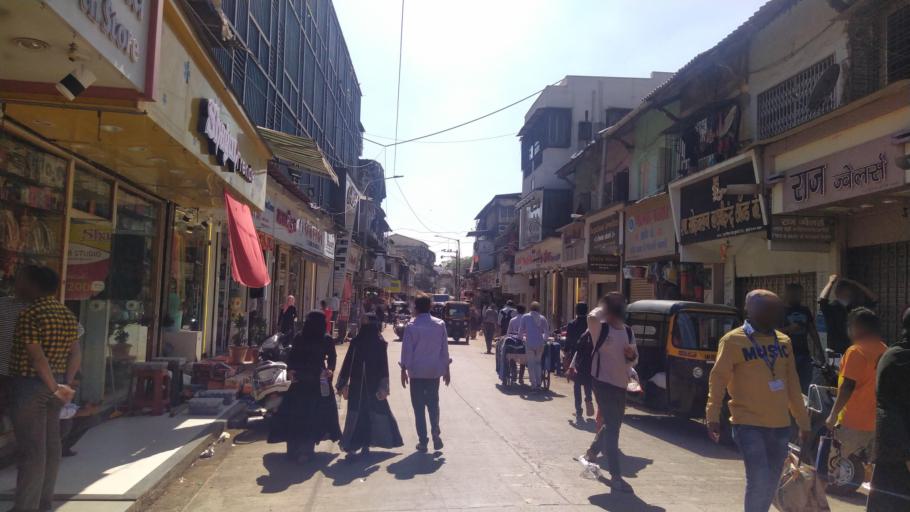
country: IN
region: Maharashtra
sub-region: Mumbai Suburban
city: Mumbai
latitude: 19.0674
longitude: 72.8779
